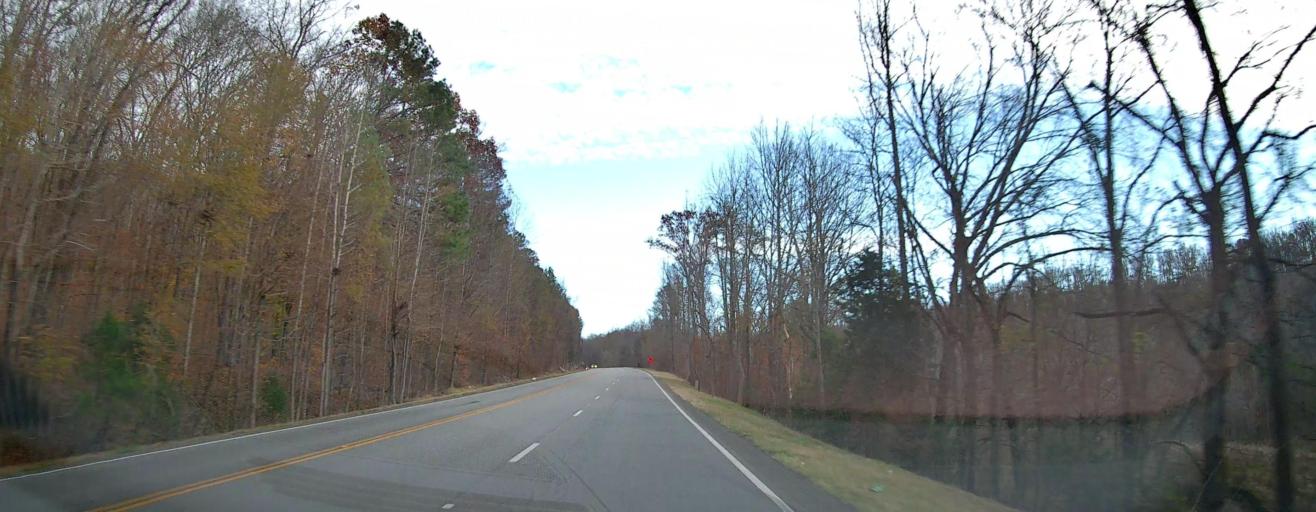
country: US
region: Alabama
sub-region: Marshall County
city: Arab
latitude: 34.3637
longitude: -86.6333
